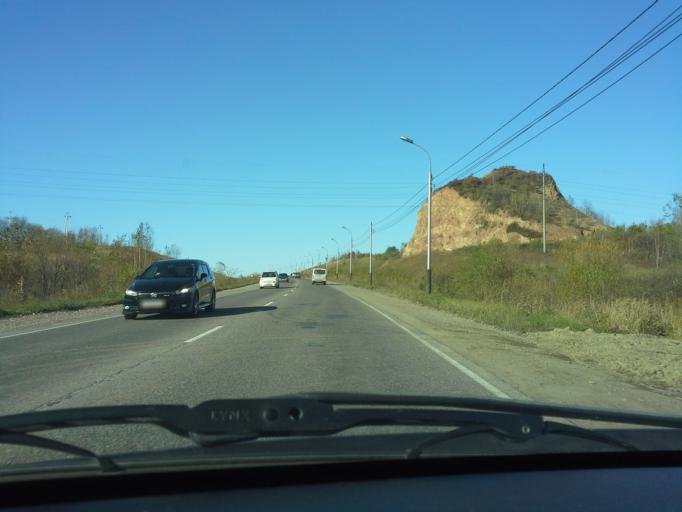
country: RU
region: Khabarovsk Krai
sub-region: Khabarovskiy Rayon
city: Khabarovsk
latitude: 48.5499
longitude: 135.0826
